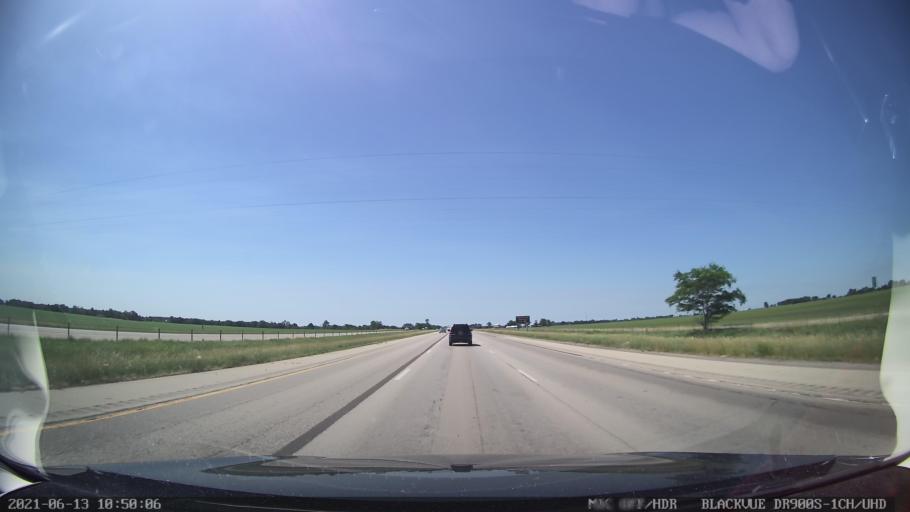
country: US
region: Illinois
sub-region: Sangamon County
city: Divernon
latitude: 39.6081
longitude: -89.6443
